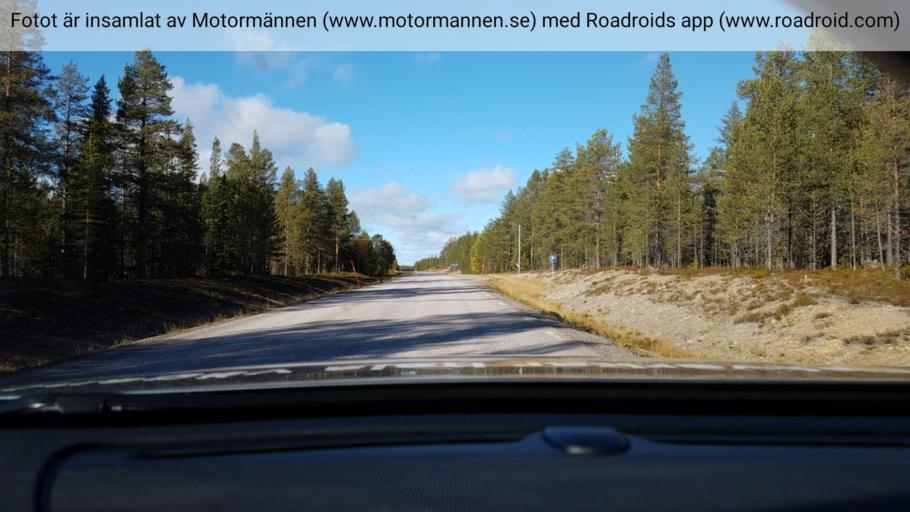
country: SE
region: Norrbotten
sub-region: Arvidsjaurs Kommun
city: Arvidsjaur
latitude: 65.7277
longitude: 18.6665
